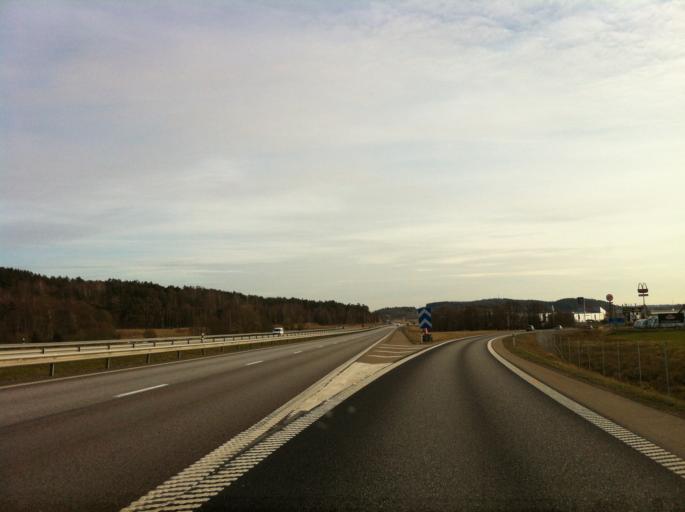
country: SE
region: Halland
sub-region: Kungsbacka Kommun
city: Fjaeras kyrkby
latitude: 57.3923
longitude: 12.1889
